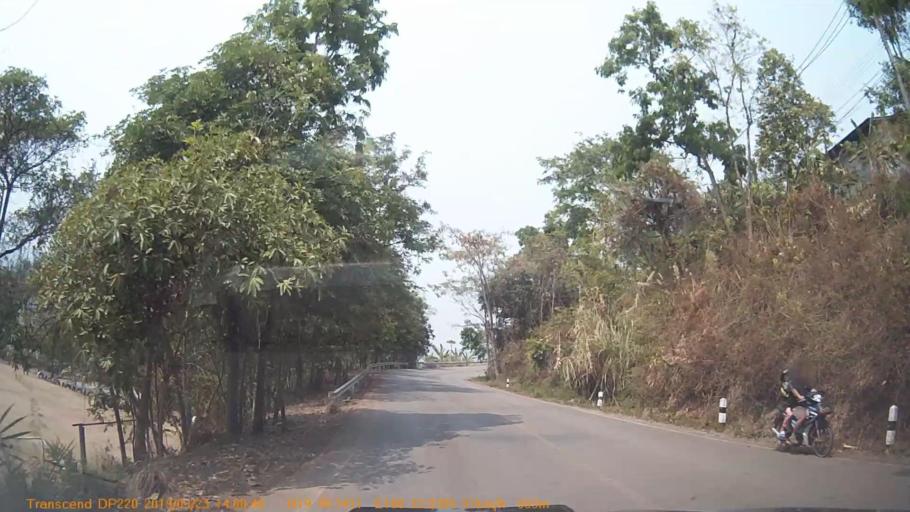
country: TH
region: Chiang Rai
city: Khun Tan
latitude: 19.8226
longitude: 100.3672
